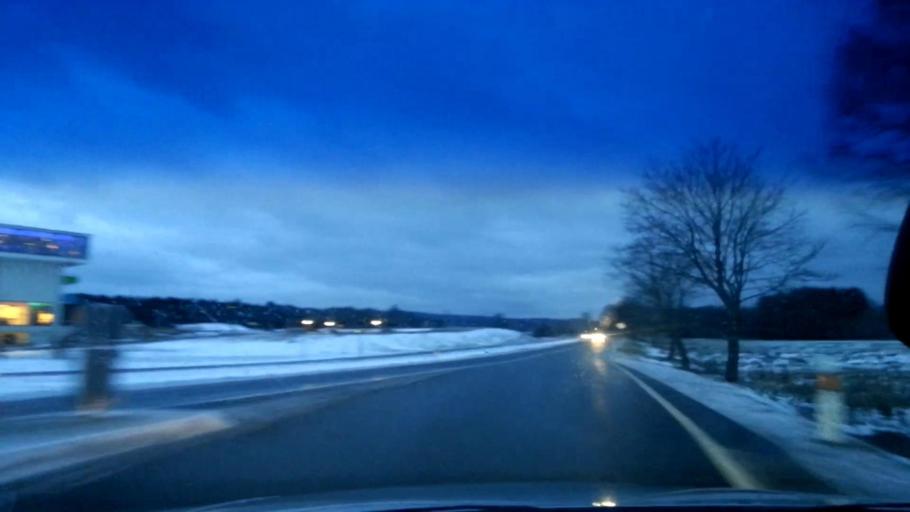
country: DE
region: Bavaria
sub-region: Upper Franconia
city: Weissenstadt
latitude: 50.0953
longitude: 11.8707
